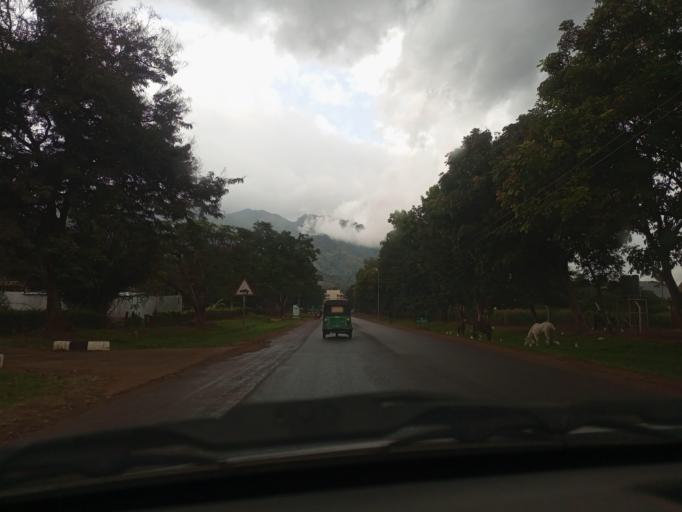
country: TZ
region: Morogoro
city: Morogoro
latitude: -6.8479
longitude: 37.6577
